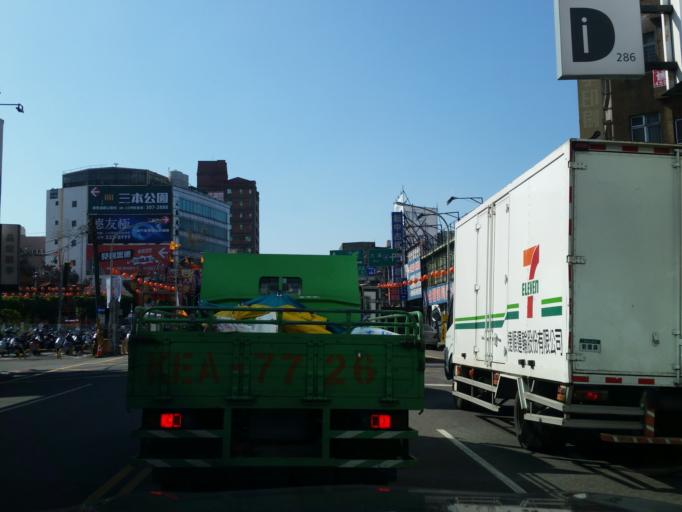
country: TW
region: Taiwan
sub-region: Taoyuan
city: Taoyuan
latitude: 24.9891
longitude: 121.3078
